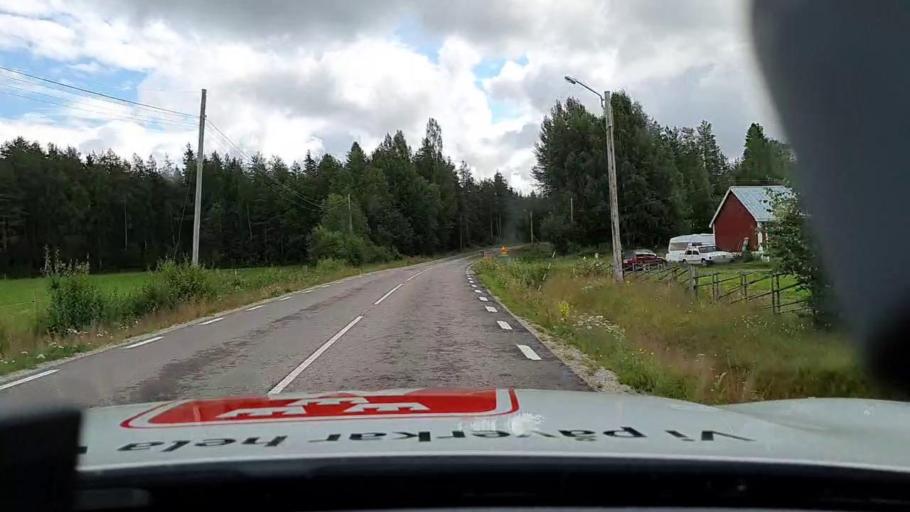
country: SE
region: Norrbotten
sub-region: Overkalix Kommun
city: OEverkalix
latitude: 66.2593
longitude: 22.8486
